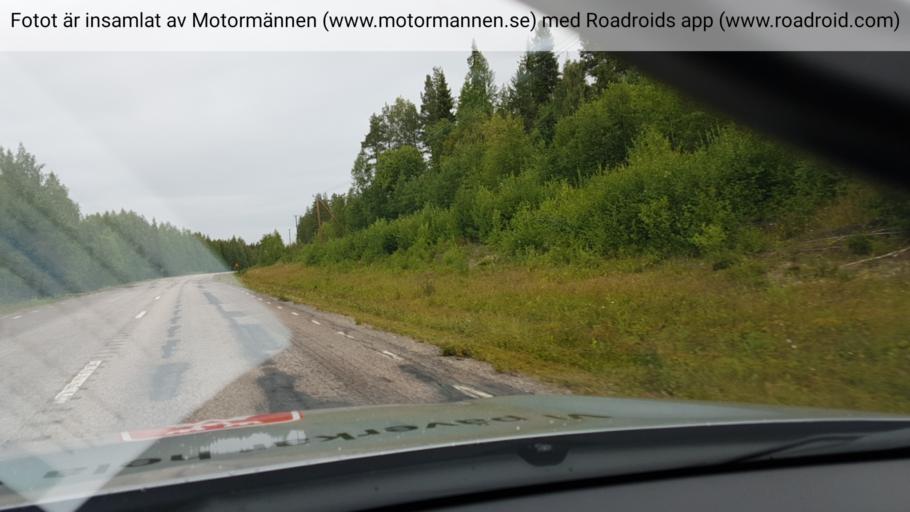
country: SE
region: Norrbotten
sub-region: Alvsbyns Kommun
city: AElvsbyn
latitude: 66.1651
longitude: 20.8809
